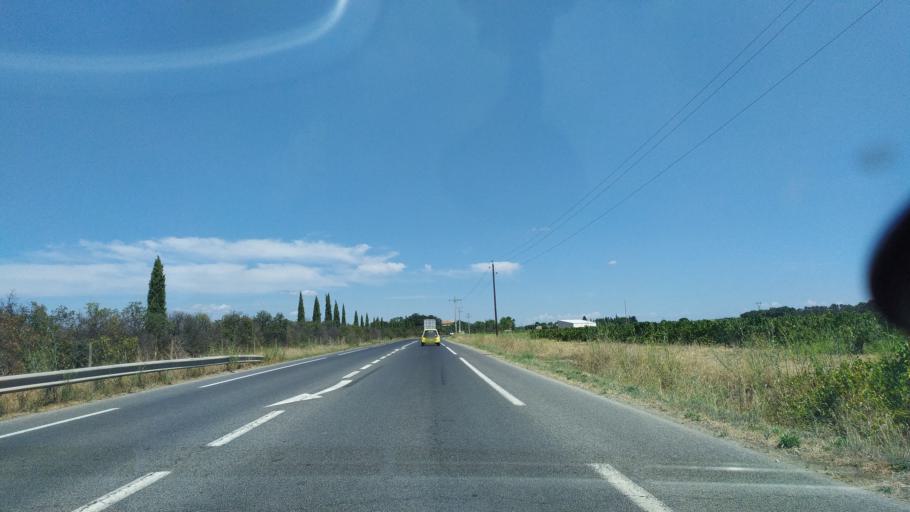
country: FR
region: Languedoc-Roussillon
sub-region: Departement du Gard
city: Aubord
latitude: 43.7626
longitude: 4.3170
